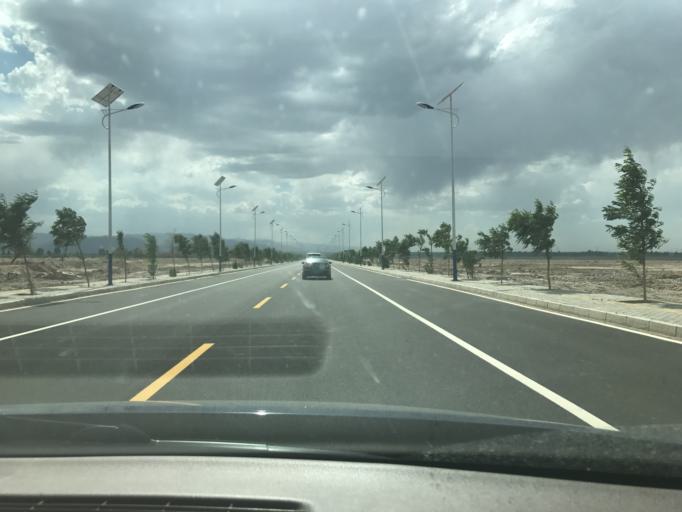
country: CN
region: Gansu Sheng
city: Wuwei
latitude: 38.1032
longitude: 102.4339
